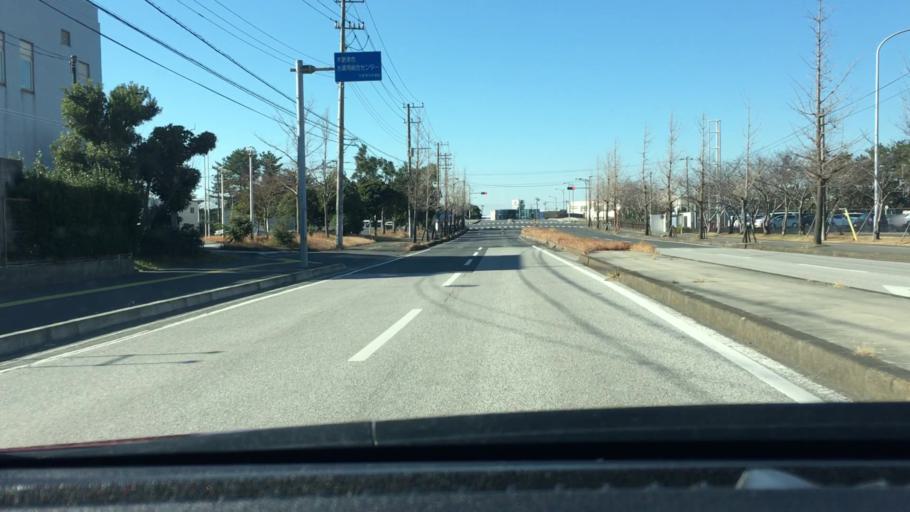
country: JP
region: Chiba
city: Kisarazu
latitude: 35.3754
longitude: 139.9162
